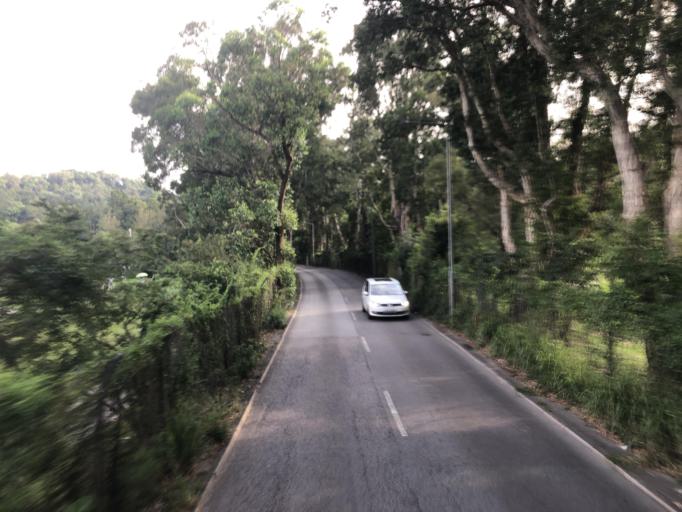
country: HK
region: Tai Po
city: Tai Po
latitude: 22.4858
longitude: 114.1156
